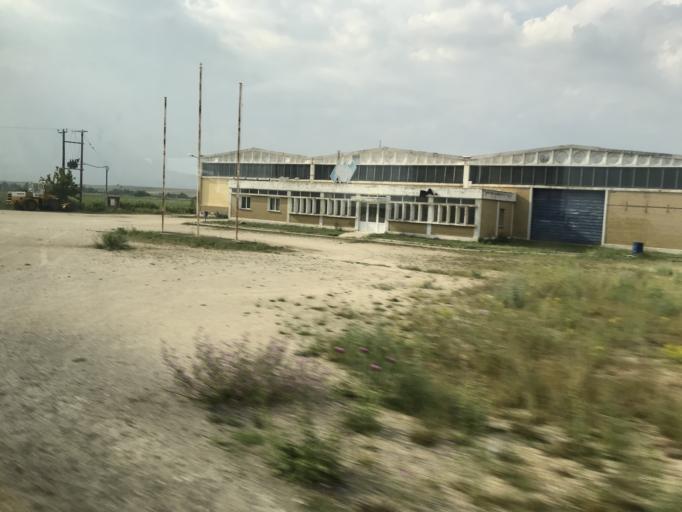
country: GR
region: East Macedonia and Thrace
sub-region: Nomos Rodopis
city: Lykeio
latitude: 41.0407
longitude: 25.6600
